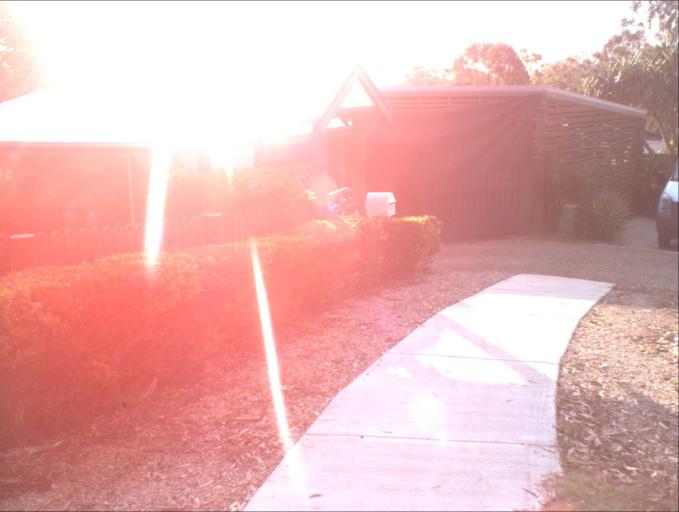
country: AU
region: Queensland
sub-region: Logan
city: Beenleigh
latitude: -27.6746
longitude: 153.2001
